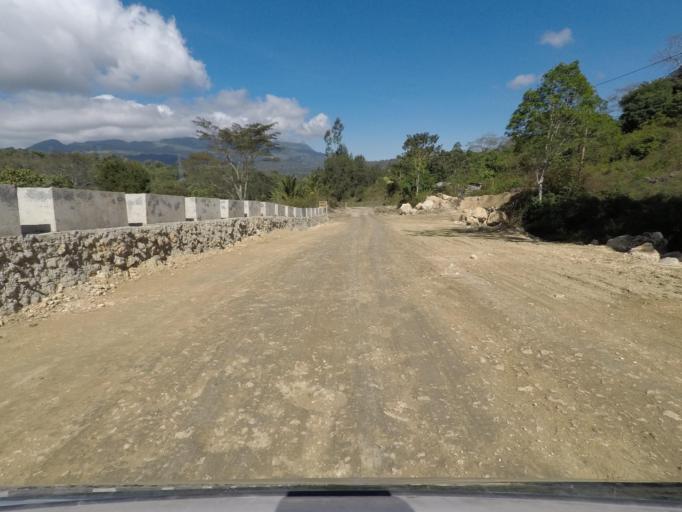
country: TL
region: Baucau
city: Venilale
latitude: -8.6640
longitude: 126.3710
